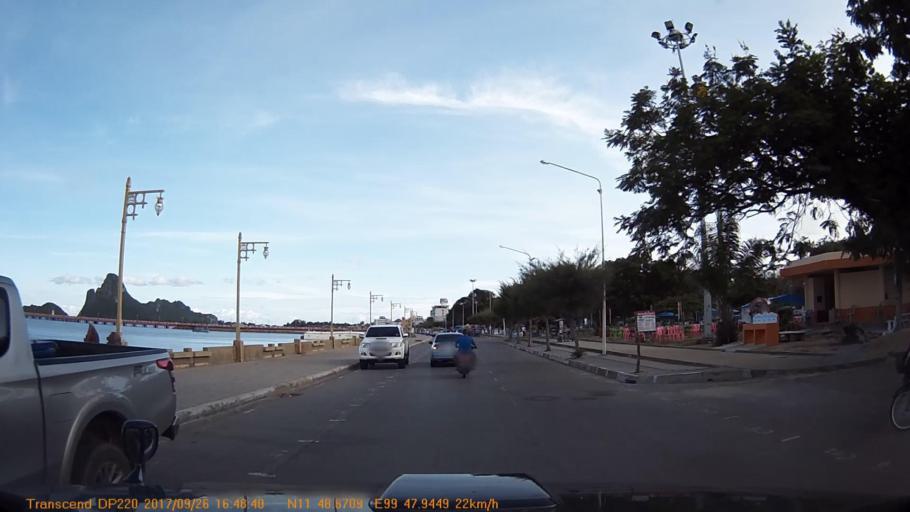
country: TH
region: Prachuap Khiri Khan
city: Prachuap Khiri Khan
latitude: 11.8111
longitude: 99.7991
